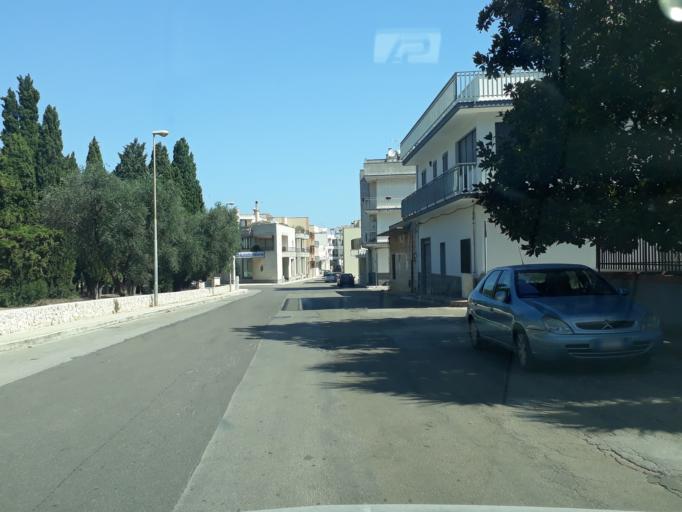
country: IT
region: Apulia
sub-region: Provincia di Brindisi
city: Carovigno
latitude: 40.7117
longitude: 17.6566
